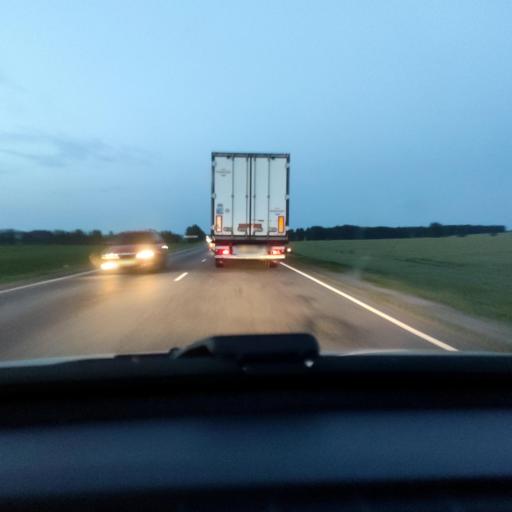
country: RU
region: Voronezj
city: Verkhnyaya Khava
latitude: 51.6799
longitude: 39.8955
